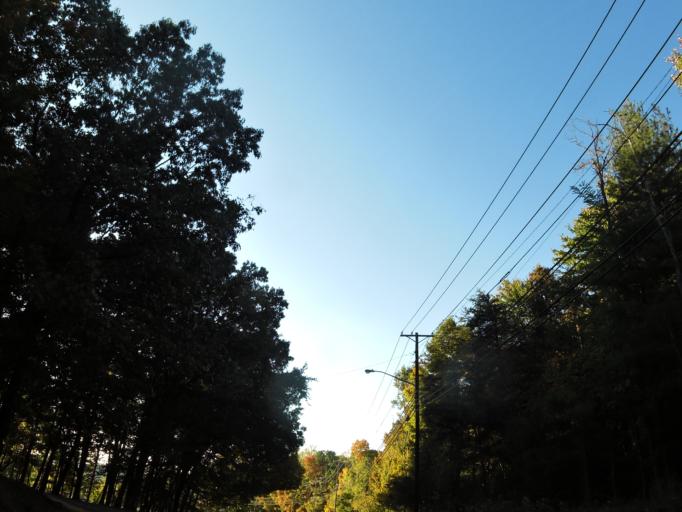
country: US
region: Tennessee
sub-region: Knox County
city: Knoxville
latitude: 36.0180
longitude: -83.9829
